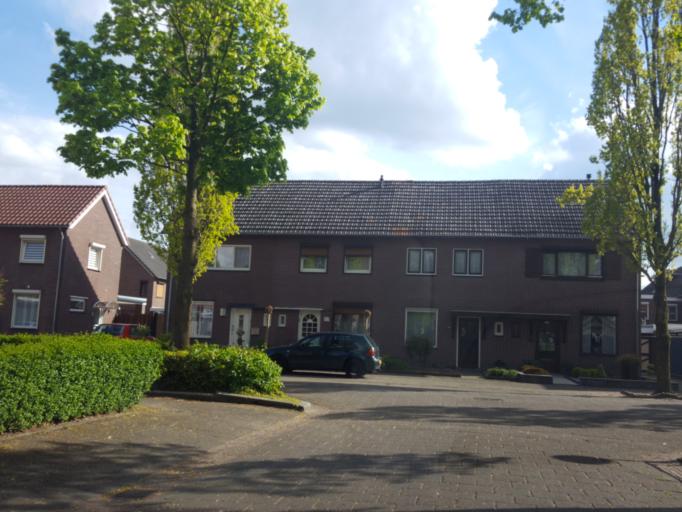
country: NL
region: Limburg
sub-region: Gemeente Weert
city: Weert
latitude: 51.2516
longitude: 5.6985
